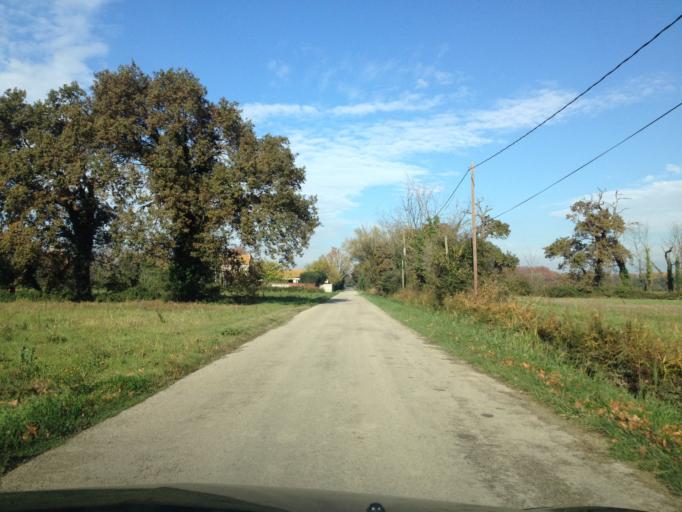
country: FR
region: Provence-Alpes-Cote d'Azur
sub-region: Departement du Vaucluse
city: Bedarrides
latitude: 44.0609
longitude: 4.8941
